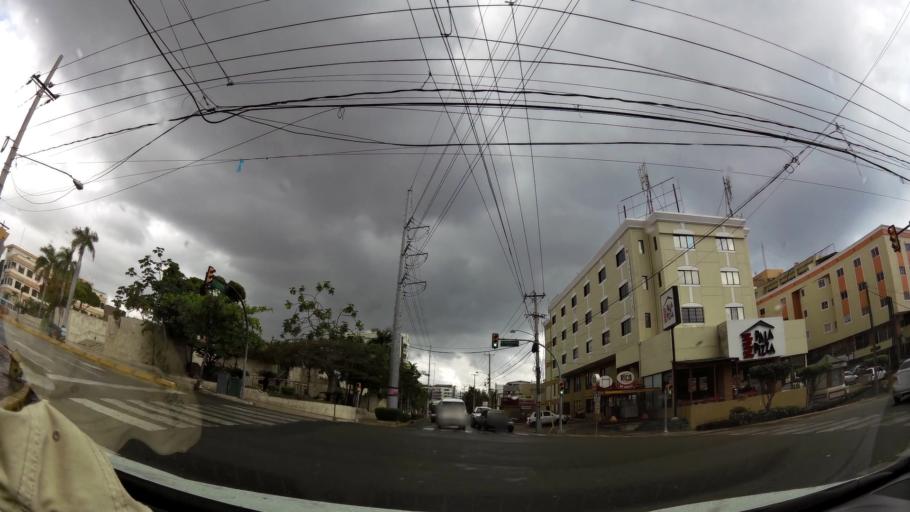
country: DO
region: Nacional
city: Ciudad Nueva
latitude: 18.4666
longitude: -69.9111
